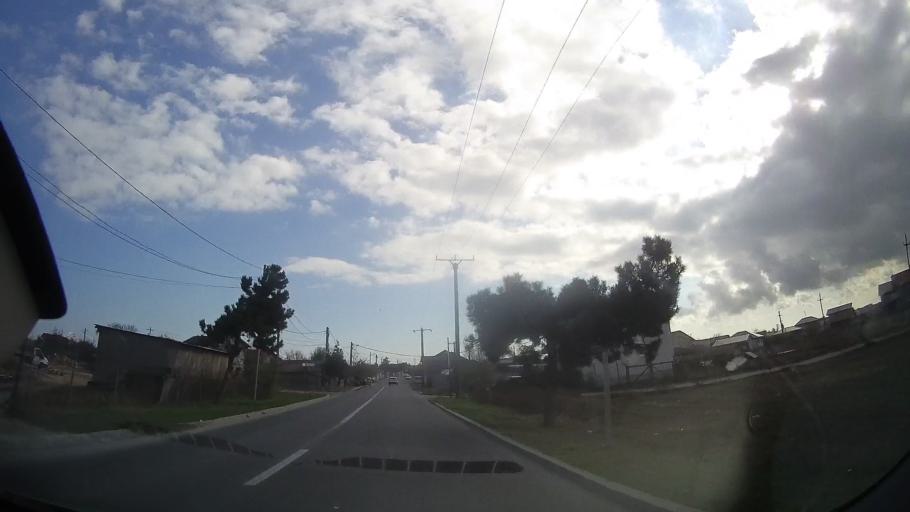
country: RO
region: Constanta
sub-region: Oras Techirghiol
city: Techirghiol
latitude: 44.0634
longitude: 28.5963
